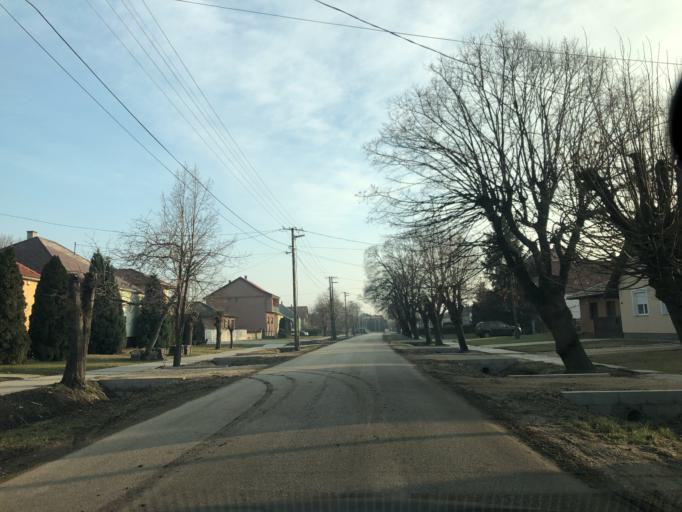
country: HU
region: Gyor-Moson-Sopron
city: Kapuvar
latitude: 47.5911
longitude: 17.0204
